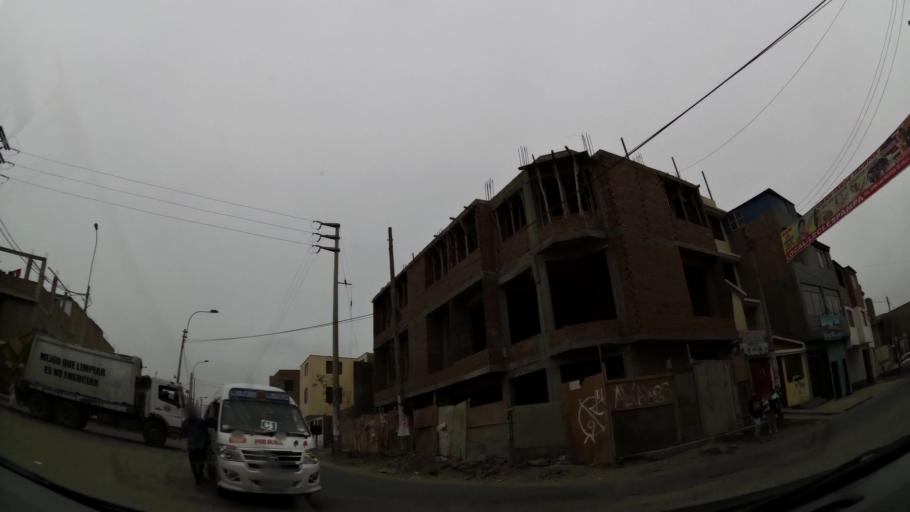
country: PE
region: Lima
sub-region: Lima
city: Surco
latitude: -12.1866
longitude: -76.9806
